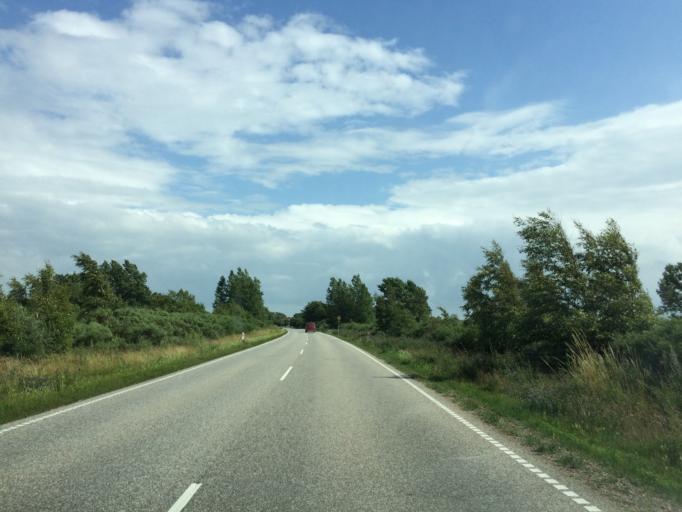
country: DK
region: Zealand
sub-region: Odsherred Kommune
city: Asnaes
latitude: 55.9650
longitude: 11.3623
